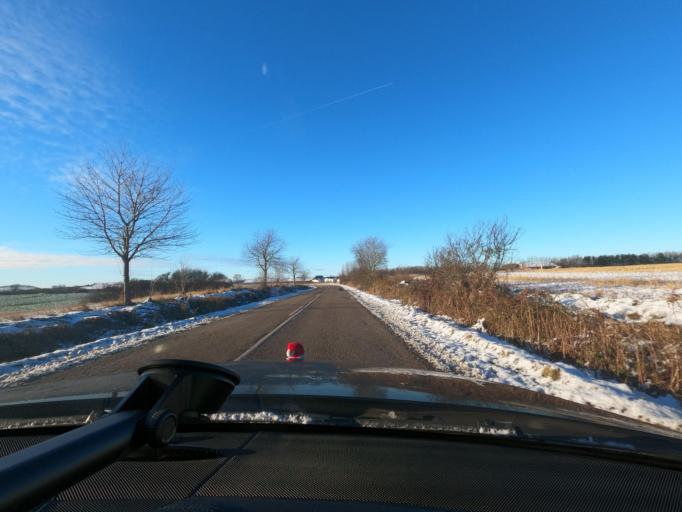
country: DK
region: South Denmark
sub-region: Sonderborg Kommune
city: Horuphav
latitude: 54.8802
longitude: 9.9044
